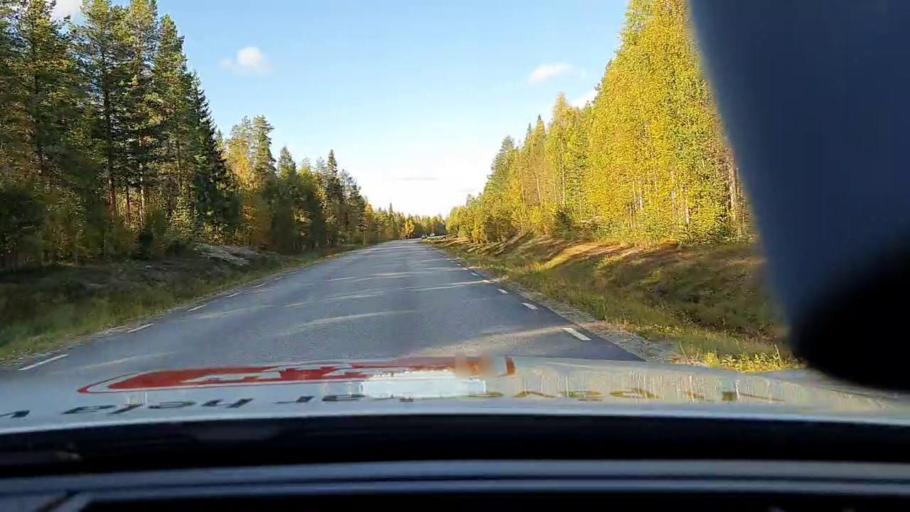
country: SE
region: Norrbotten
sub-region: Pitea Kommun
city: Norrfjarden
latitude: 65.4982
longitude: 21.4755
